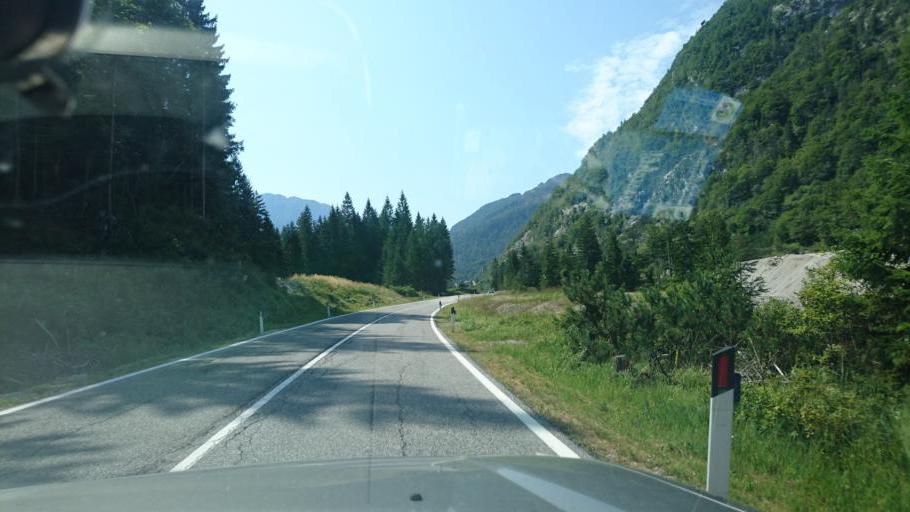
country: IT
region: Friuli Venezia Giulia
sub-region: Provincia di Udine
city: Tarvisio
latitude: 46.4501
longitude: 13.5750
